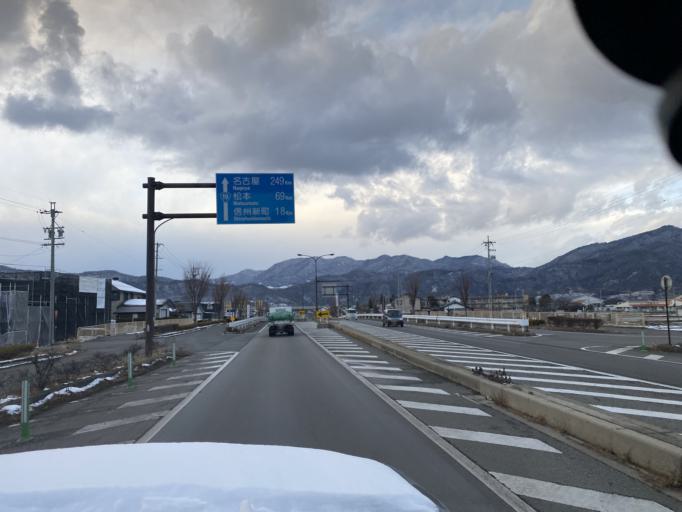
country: JP
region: Nagano
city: Nagano-shi
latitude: 36.6061
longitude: 138.1545
